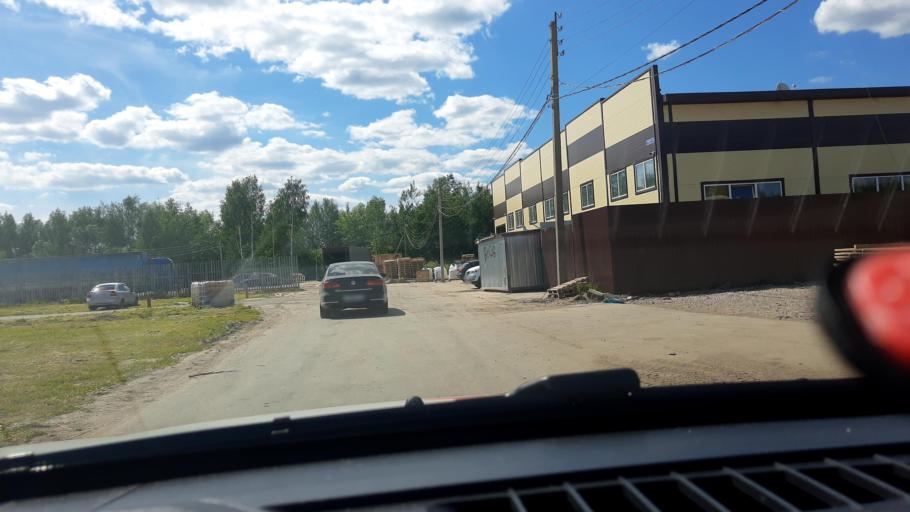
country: RU
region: Nizjnij Novgorod
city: Gorbatovka
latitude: 56.3024
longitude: 43.8067
